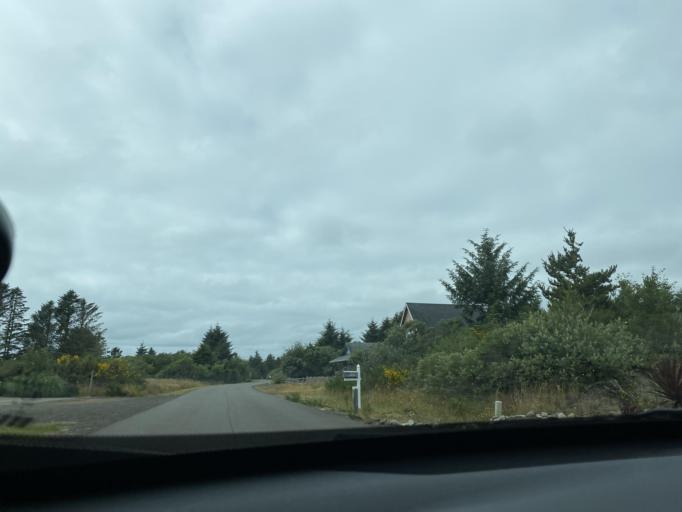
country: US
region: Washington
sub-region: Grays Harbor County
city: Ocean Shores
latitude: 46.9513
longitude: -124.1436
